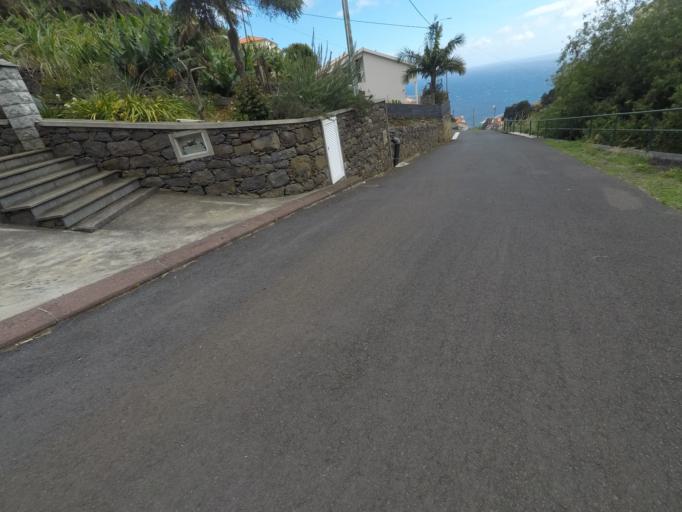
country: PT
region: Madeira
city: Calheta
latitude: 32.7271
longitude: -17.1772
